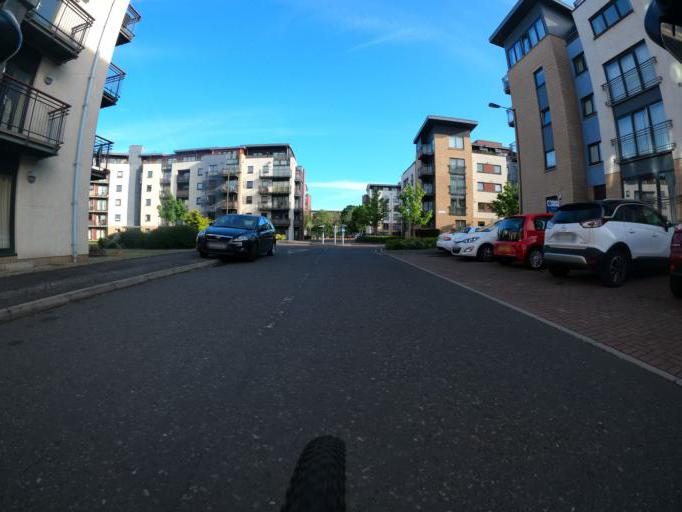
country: GB
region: Scotland
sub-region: Edinburgh
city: Edinburgh
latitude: 55.9723
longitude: -3.2266
